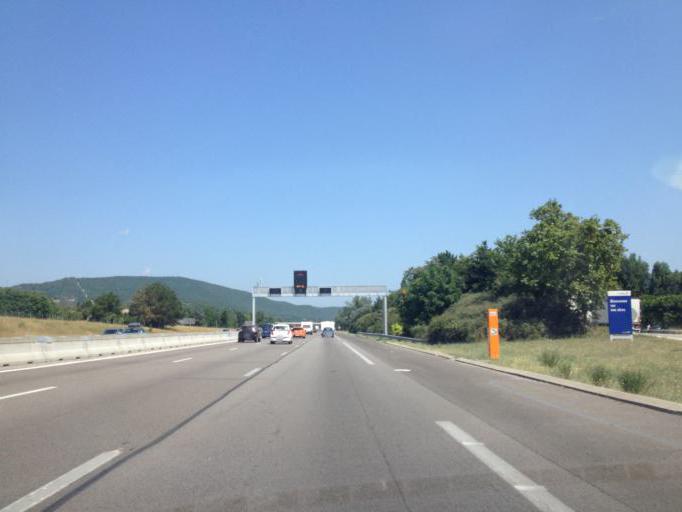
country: FR
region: Rhone-Alpes
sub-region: Departement de la Drome
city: Saint-Marcel-les-Sauzet
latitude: 44.5894
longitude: 4.8012
